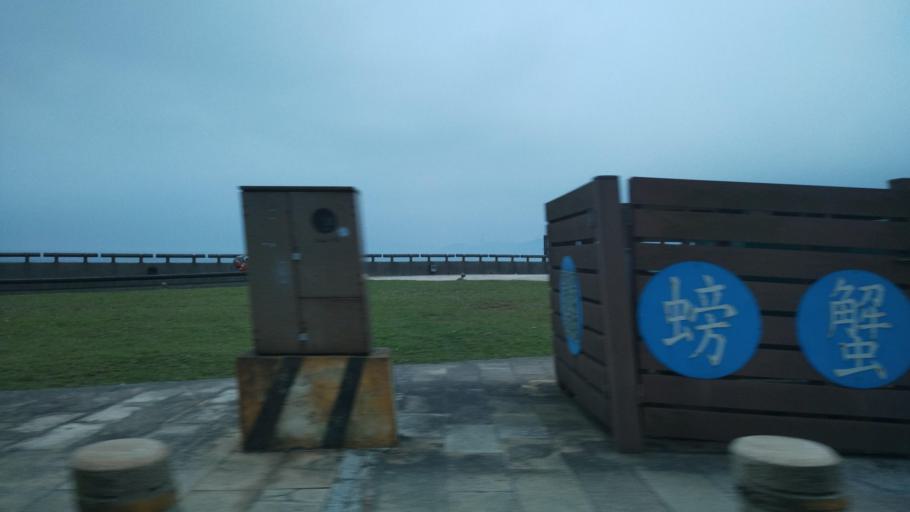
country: TW
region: Taiwan
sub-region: Keelung
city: Keelung
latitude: 25.1972
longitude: 121.6895
